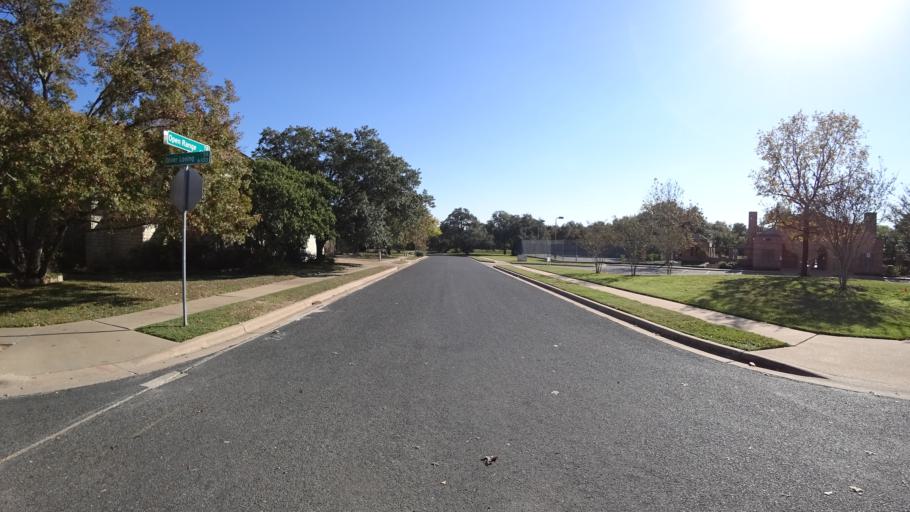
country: US
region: Texas
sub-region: Travis County
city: Shady Hollow
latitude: 30.2220
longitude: -97.8699
